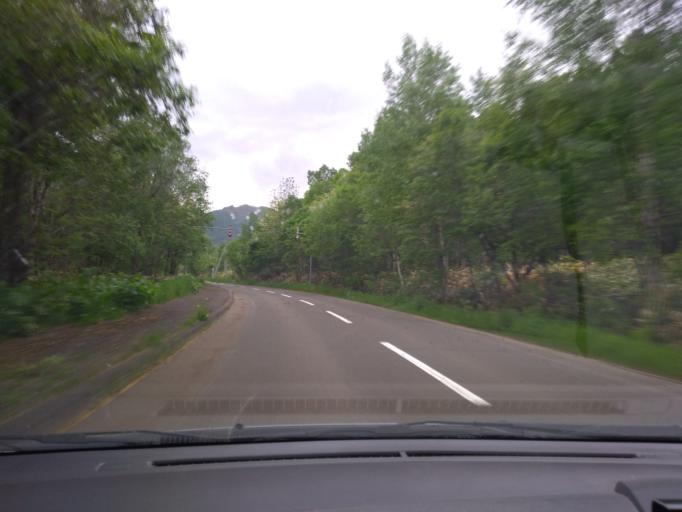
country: JP
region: Hokkaido
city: Shimo-furano
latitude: 43.1766
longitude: 142.5357
